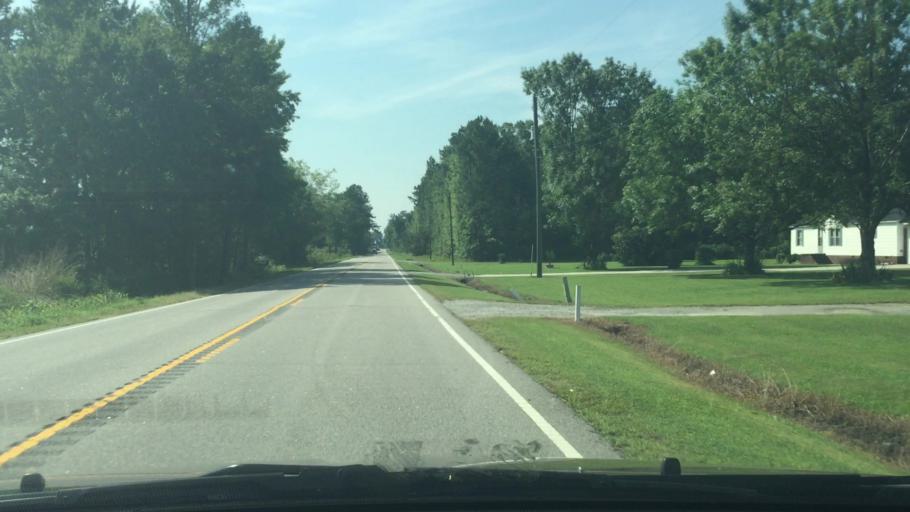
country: US
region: Virginia
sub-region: Southampton County
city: Courtland
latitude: 36.8361
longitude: -77.1287
